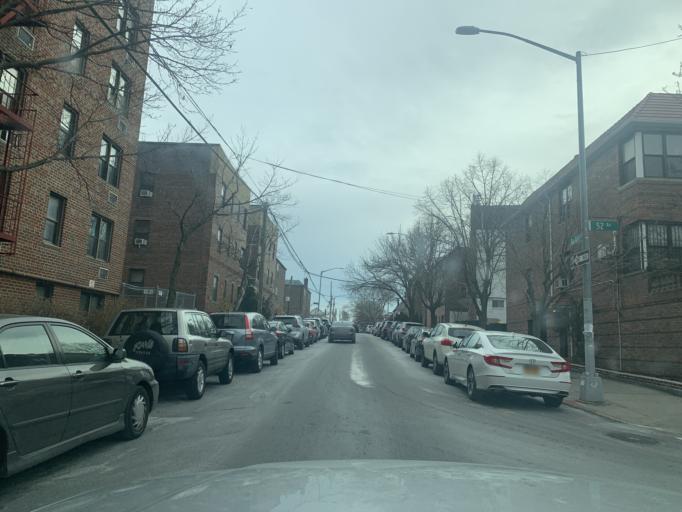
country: US
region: New York
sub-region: Kings County
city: East New York
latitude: 40.7354
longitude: -73.8802
